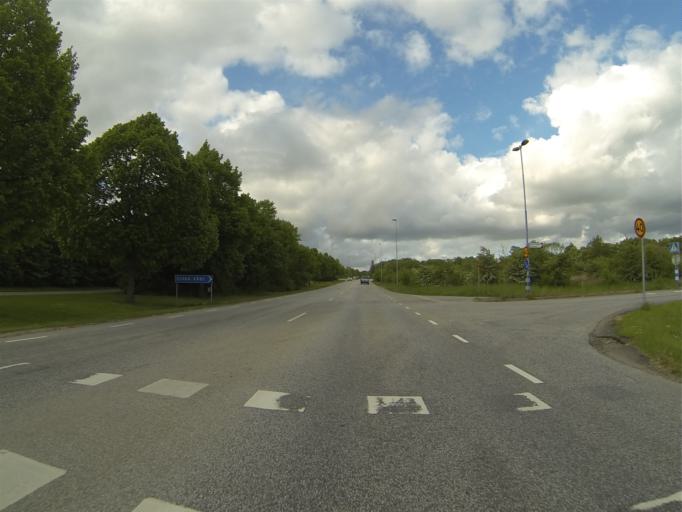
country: SE
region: Skane
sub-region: Lunds Kommun
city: Lund
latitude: 55.6935
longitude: 13.2270
